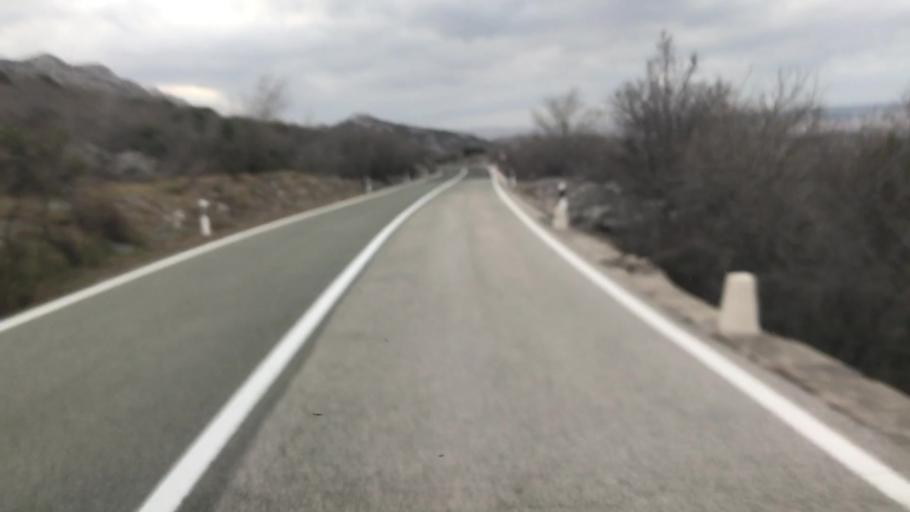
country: HR
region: Licko-Senjska
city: Novalja
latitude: 44.6732
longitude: 14.9427
